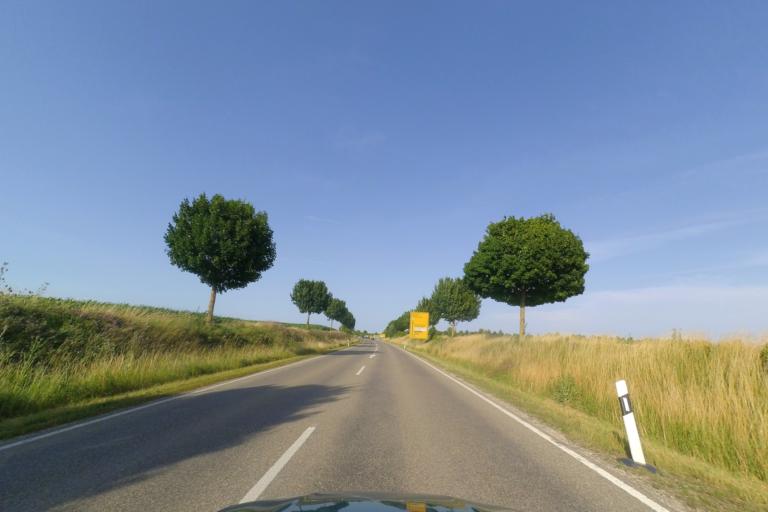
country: DE
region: Bavaria
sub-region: Swabia
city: Gundelfingen
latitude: 48.5659
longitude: 10.3935
